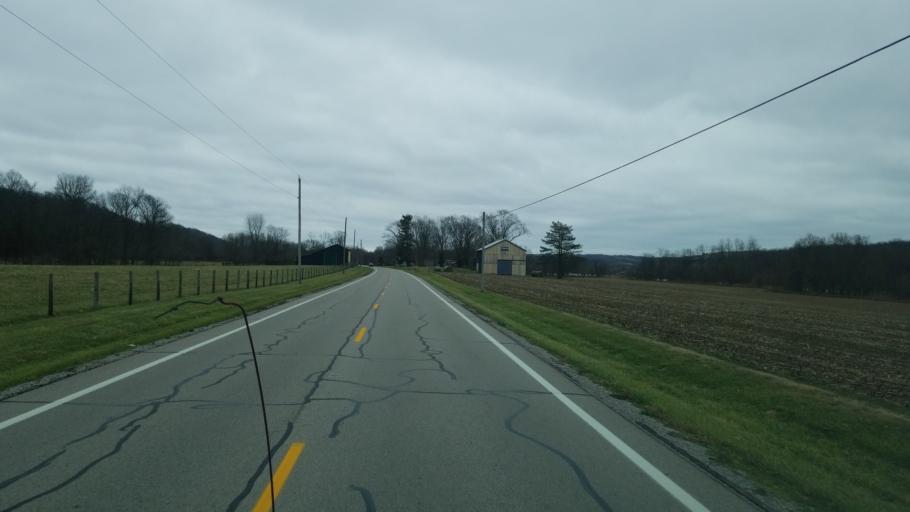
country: US
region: Ohio
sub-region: Clermont County
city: New Richmond
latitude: 38.8051
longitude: -84.2008
